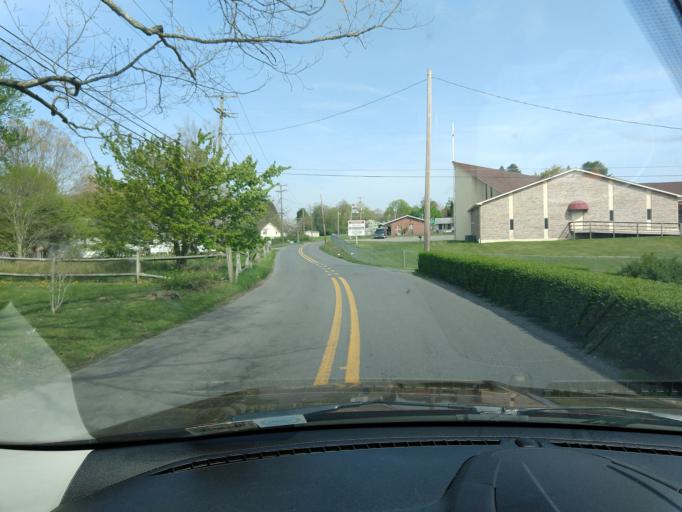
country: US
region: West Virginia
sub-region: Raleigh County
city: Crab Orchard
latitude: 37.7474
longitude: -81.2352
